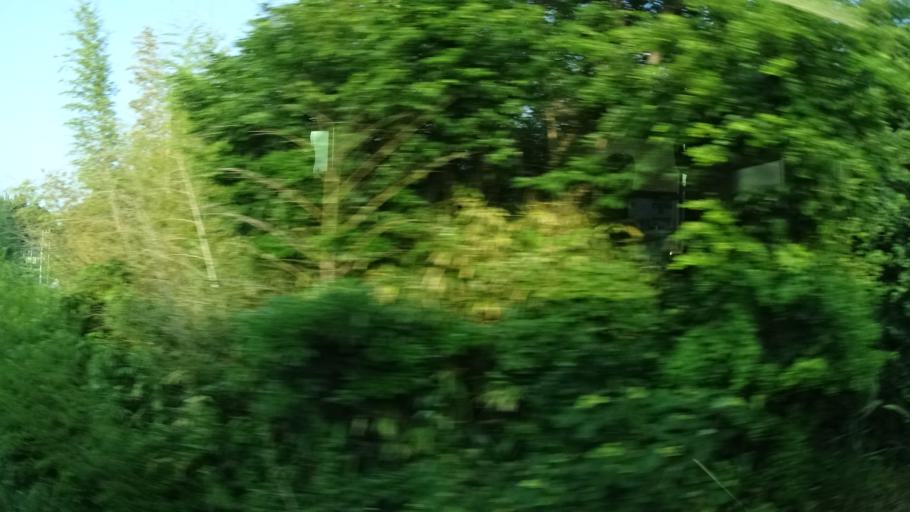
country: JP
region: Ibaraki
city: Funaishikawa
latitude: 36.5247
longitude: 140.6210
